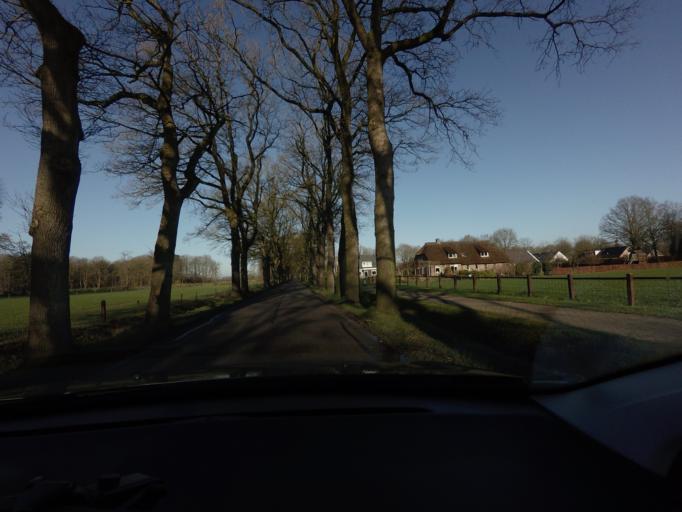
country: NL
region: Drenthe
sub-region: Gemeente Assen
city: Assen
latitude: 52.8546
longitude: 6.5980
